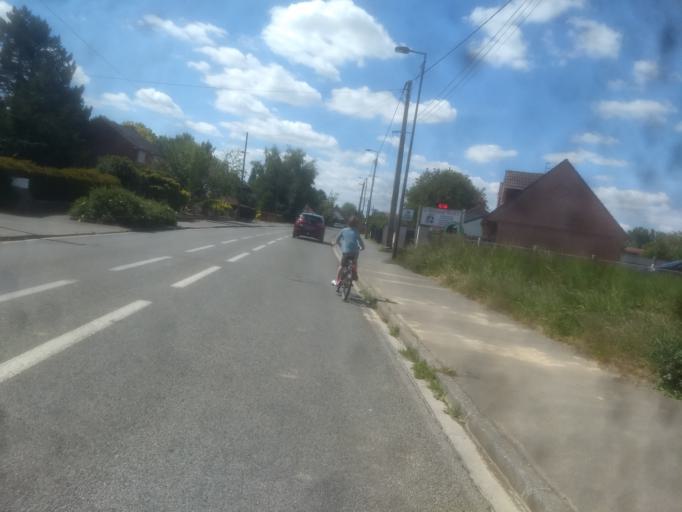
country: FR
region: Nord-Pas-de-Calais
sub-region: Departement du Pas-de-Calais
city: Agny
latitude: 50.2504
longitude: 2.7307
